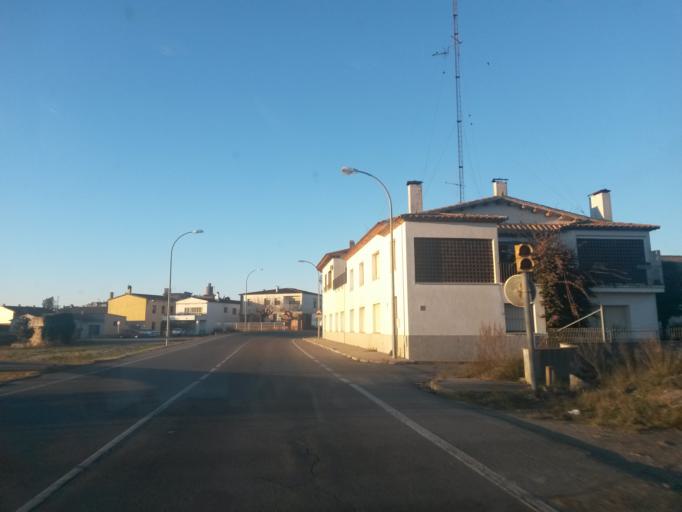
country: ES
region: Catalonia
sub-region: Provincia de Girona
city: Pals
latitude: 41.9672
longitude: 3.1488
